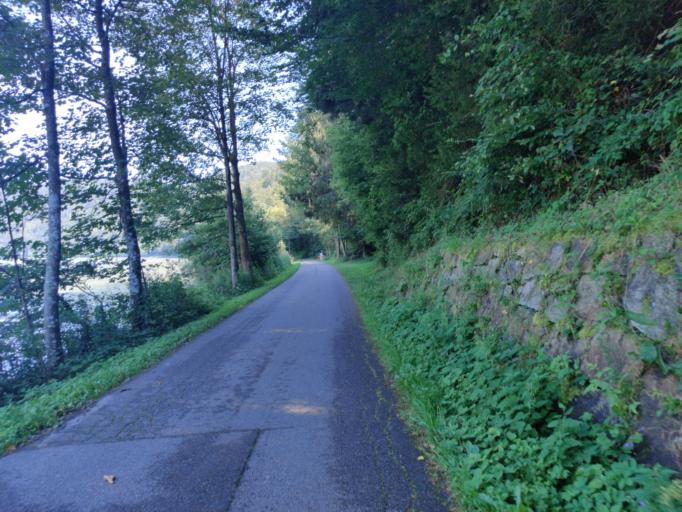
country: AT
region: Upper Austria
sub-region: Politischer Bezirk Rohrbach
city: Atzesberg
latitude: 48.4441
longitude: 13.8742
